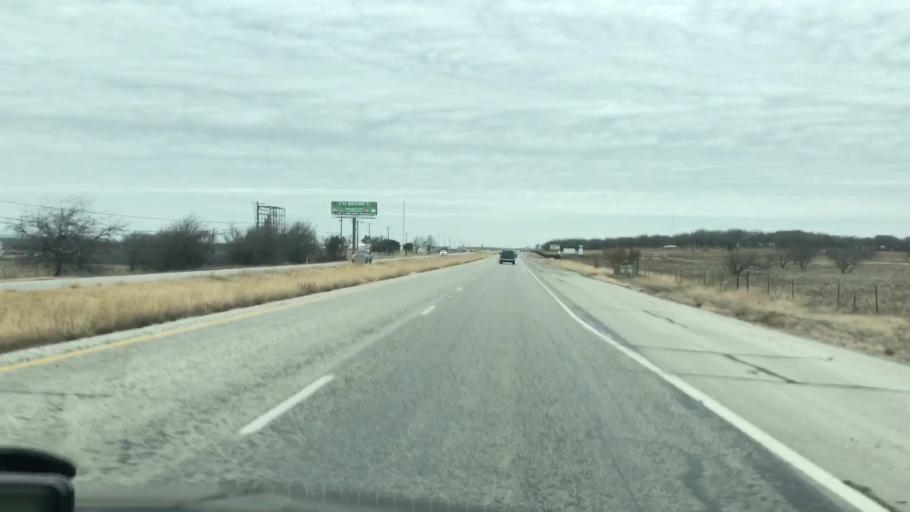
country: US
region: Texas
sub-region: Jack County
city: Jacksboro
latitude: 33.1919
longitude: -98.1384
